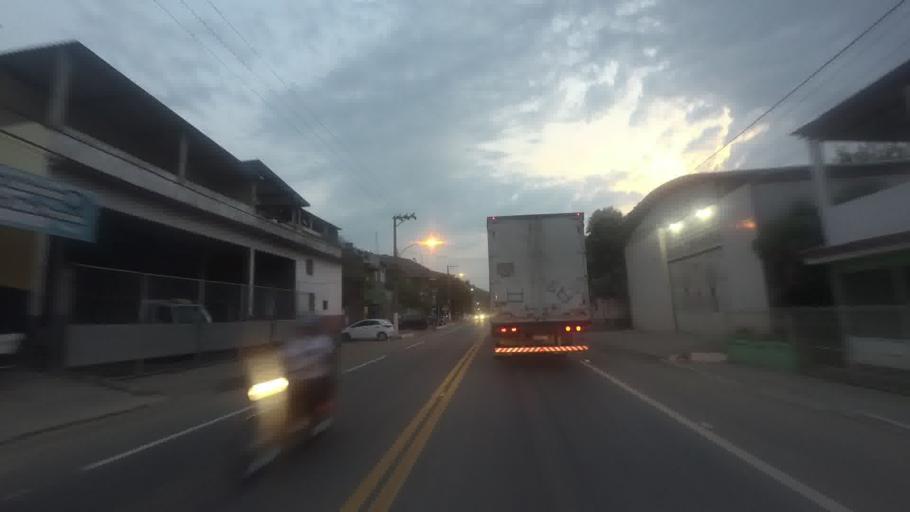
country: BR
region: Minas Gerais
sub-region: Alem Paraiba
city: Alem Paraiba
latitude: -21.8910
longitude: -42.7058
